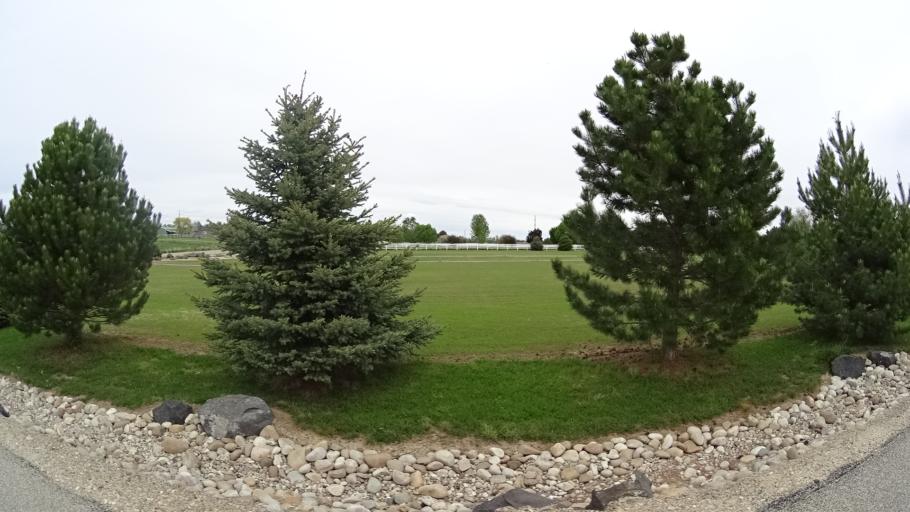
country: US
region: Idaho
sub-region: Ada County
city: Kuna
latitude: 43.4968
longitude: -116.3394
